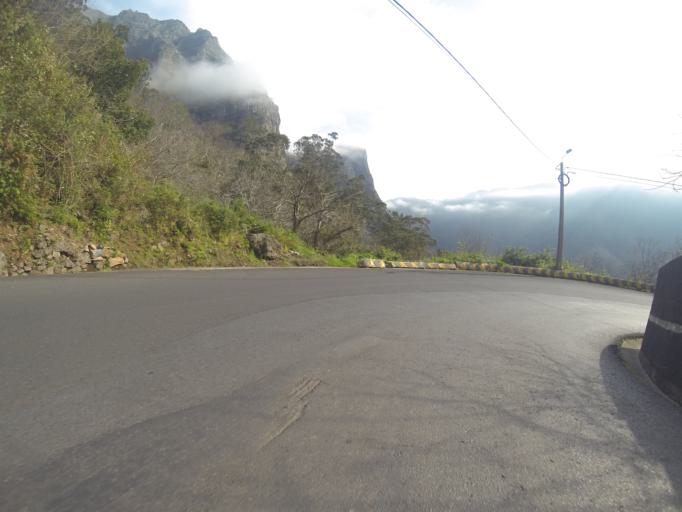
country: PT
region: Madeira
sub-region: Camara de Lobos
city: Curral das Freiras
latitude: 32.7207
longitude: -16.9631
